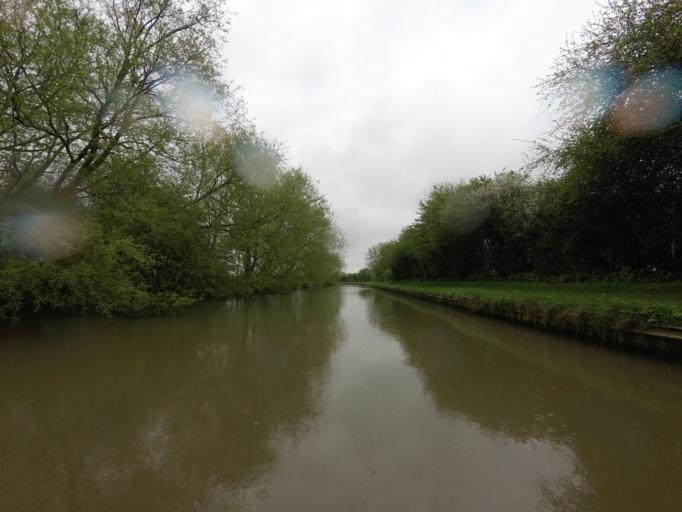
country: GB
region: England
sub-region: Northamptonshire
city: Roade
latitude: 52.1226
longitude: -0.8882
